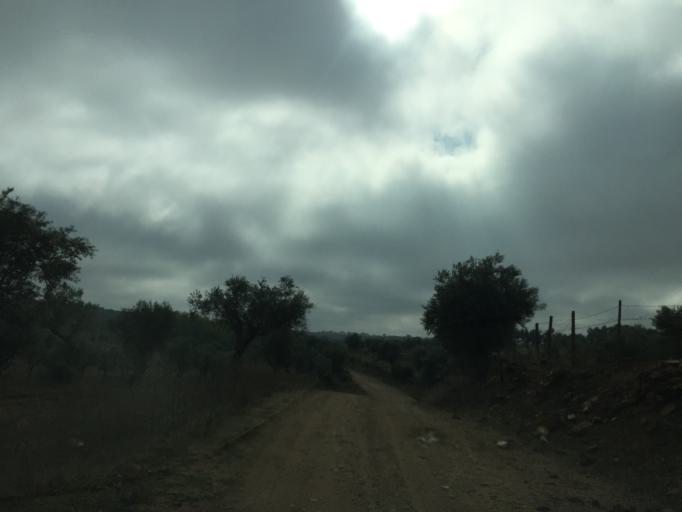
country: PT
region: Portalegre
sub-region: Fronteira
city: Fronteira
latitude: 39.0624
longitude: -7.6306
